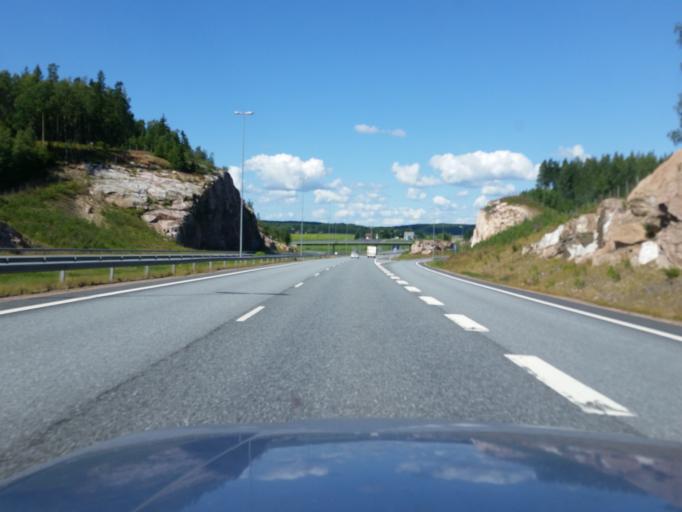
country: FI
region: Varsinais-Suomi
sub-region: Salo
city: Muurla
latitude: 60.3777
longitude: 23.3270
